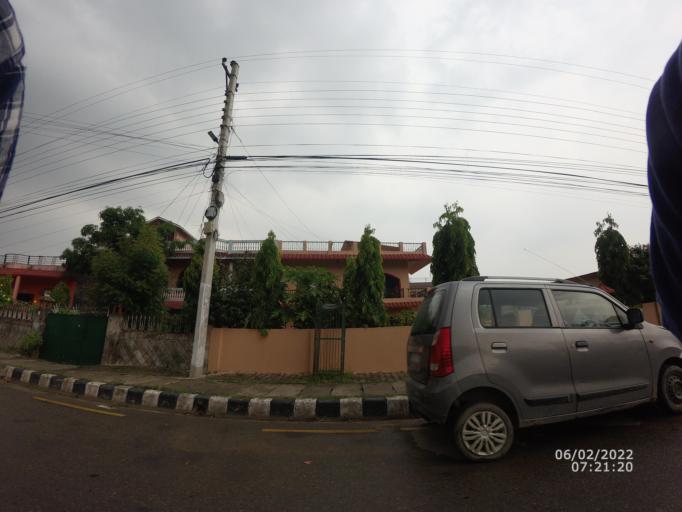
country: NP
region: Western Region
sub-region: Lumbini Zone
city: Bhairahawa
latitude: 27.4880
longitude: 83.4430
